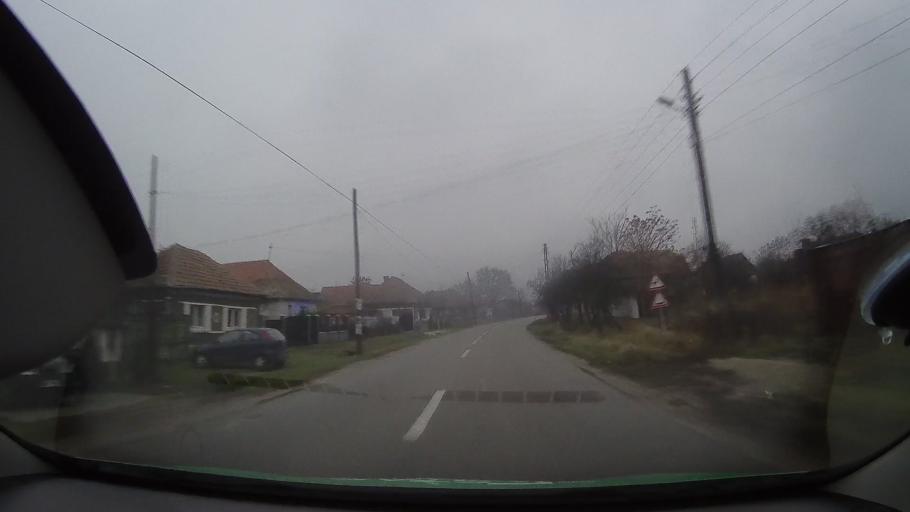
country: RO
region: Bihor
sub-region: Comuna Tulca
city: Tulca
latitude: 46.7889
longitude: 21.8151
